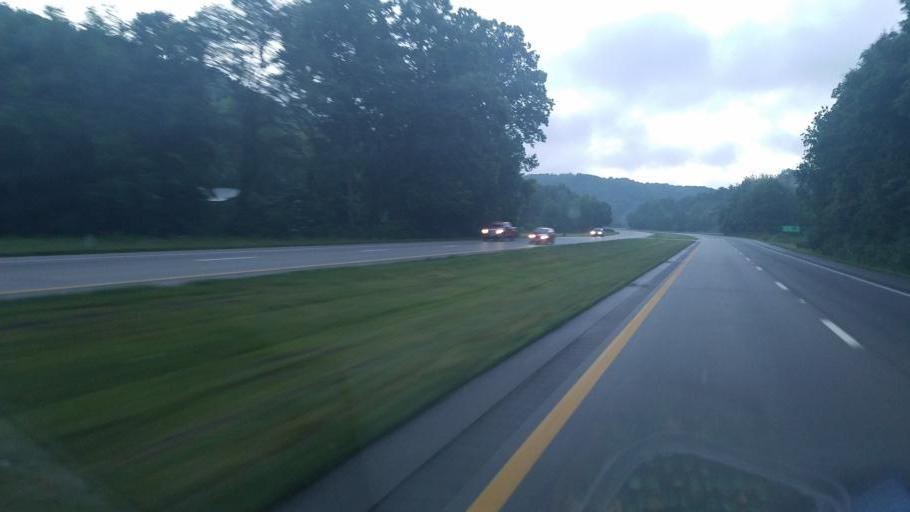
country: US
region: Ohio
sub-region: Pike County
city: Waverly
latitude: 39.1958
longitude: -82.7998
